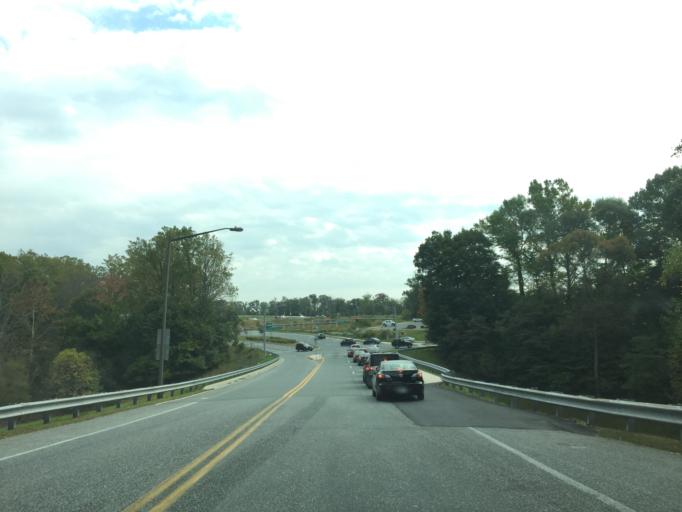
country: US
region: Maryland
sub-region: Harford County
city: Joppatowne
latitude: 39.4648
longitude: -76.3176
